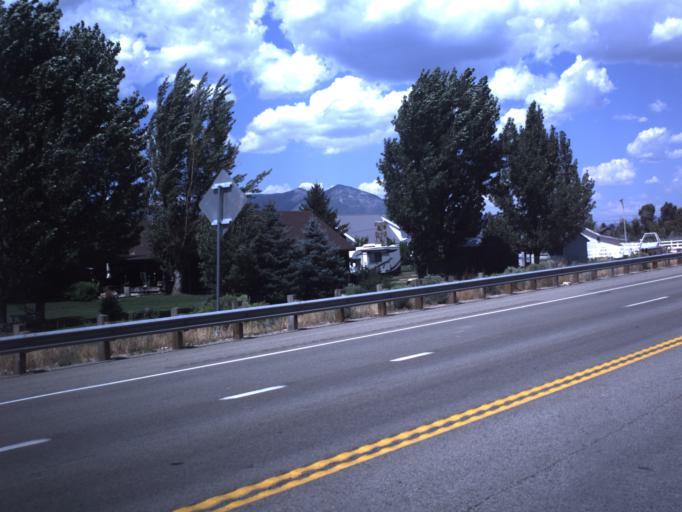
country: US
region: Utah
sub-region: Wasatch County
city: Midway
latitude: 40.4582
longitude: -111.4684
